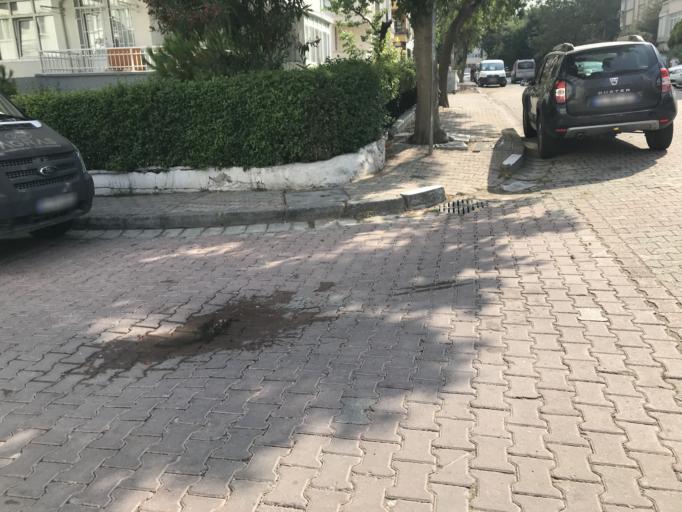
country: TR
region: Istanbul
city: Bahcelievler
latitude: 41.0004
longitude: 28.8629
